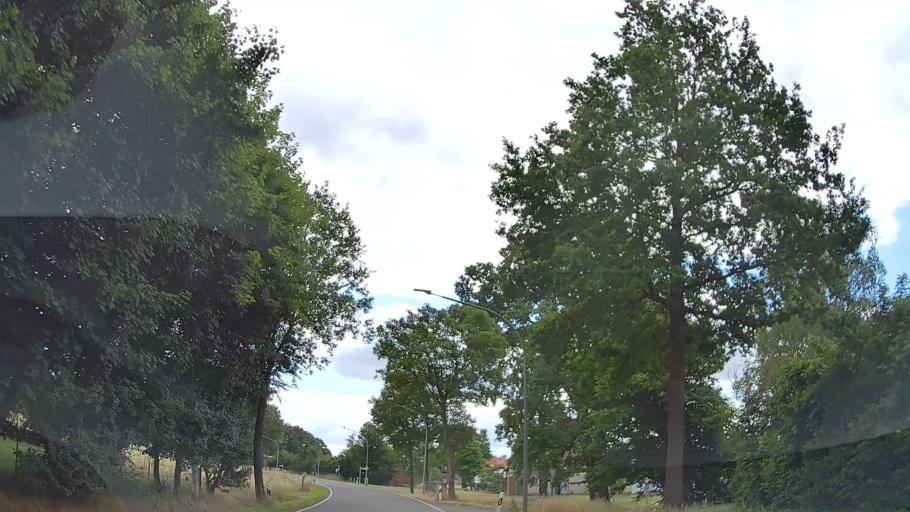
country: DE
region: Lower Saxony
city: Brockum
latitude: 52.4522
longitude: 8.4841
